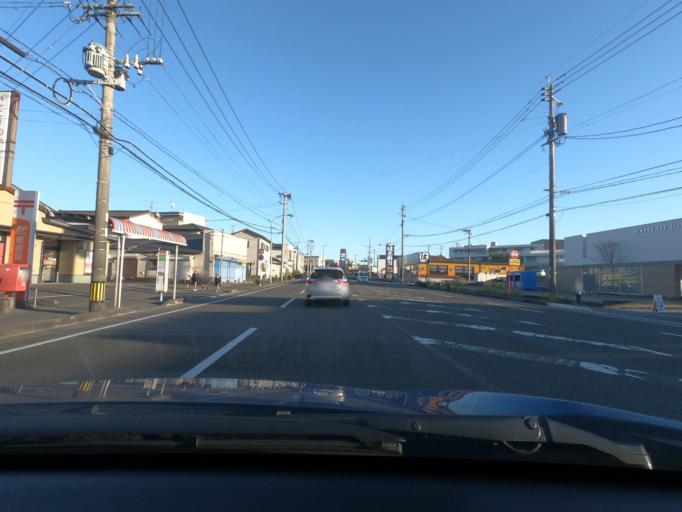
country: JP
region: Kagoshima
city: Satsumasendai
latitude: 31.8322
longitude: 130.2942
